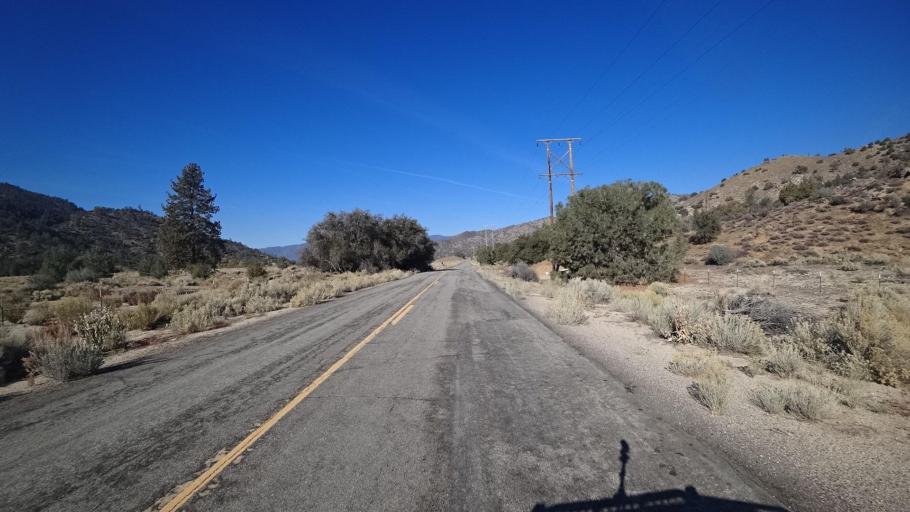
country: US
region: California
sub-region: Kern County
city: Bodfish
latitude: 35.3905
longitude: -118.4299
